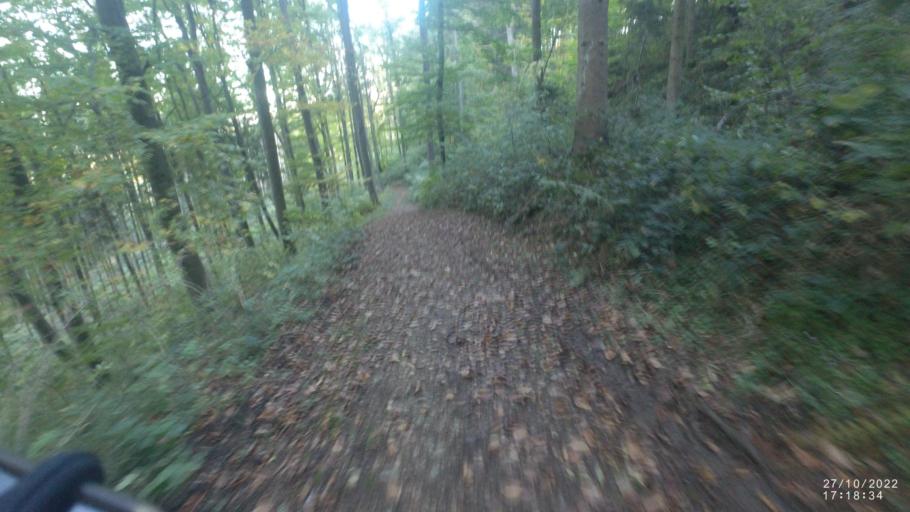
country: DE
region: Baden-Wuerttemberg
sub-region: Regierungsbezirk Stuttgart
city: Gingen an der Fils
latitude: 48.6549
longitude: 9.7611
